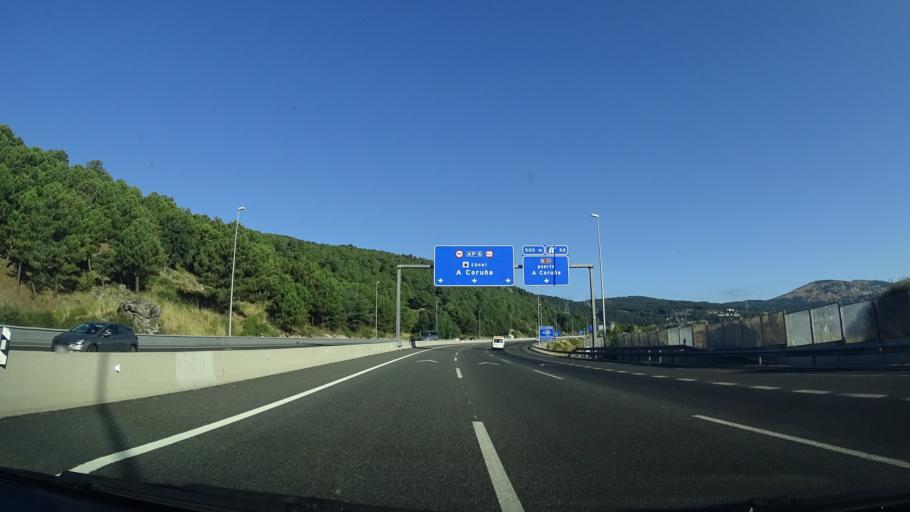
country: ES
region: Madrid
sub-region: Provincia de Madrid
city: Guadarrama
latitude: 40.6874
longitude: -4.1198
